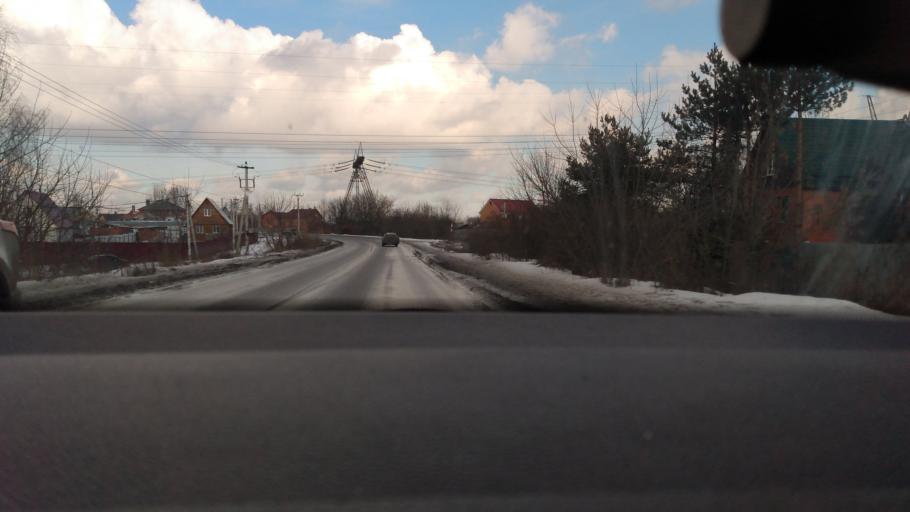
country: RU
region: Moskovskaya
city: Chornaya
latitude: 55.6998
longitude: 38.0592
